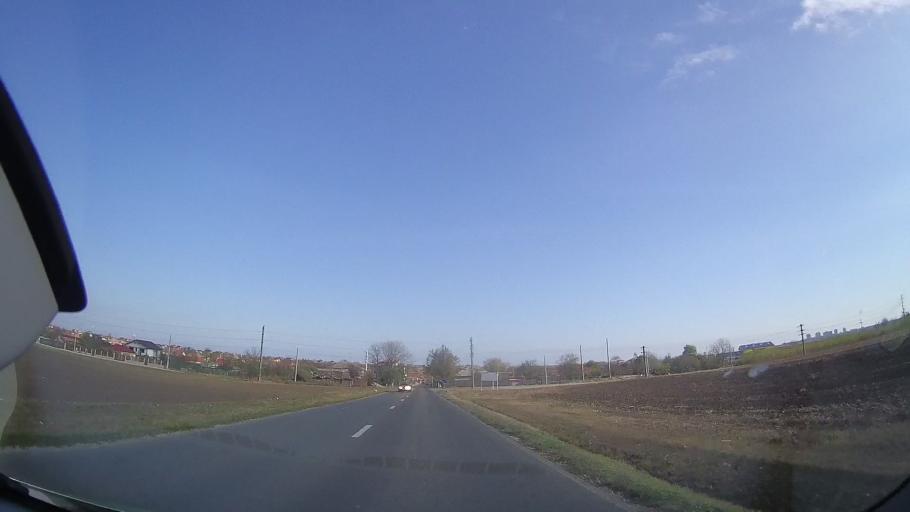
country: RO
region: Constanta
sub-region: Comuna Douazeci si Trei August
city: Douazeci si Trei August
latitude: 43.9138
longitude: 28.5761
